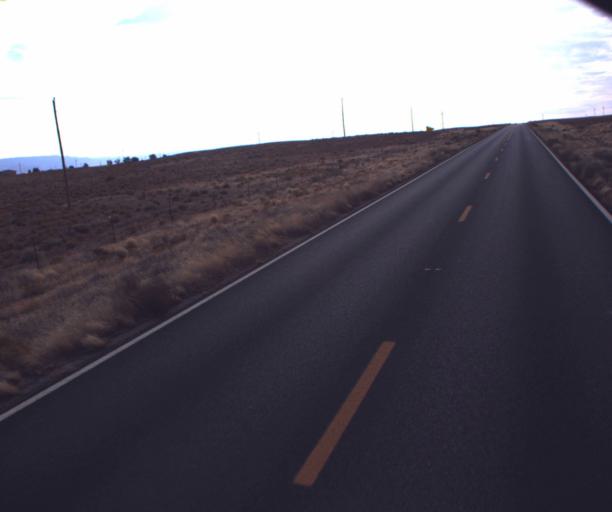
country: US
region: Arizona
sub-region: Apache County
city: Many Farms
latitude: 36.5915
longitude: -109.5628
